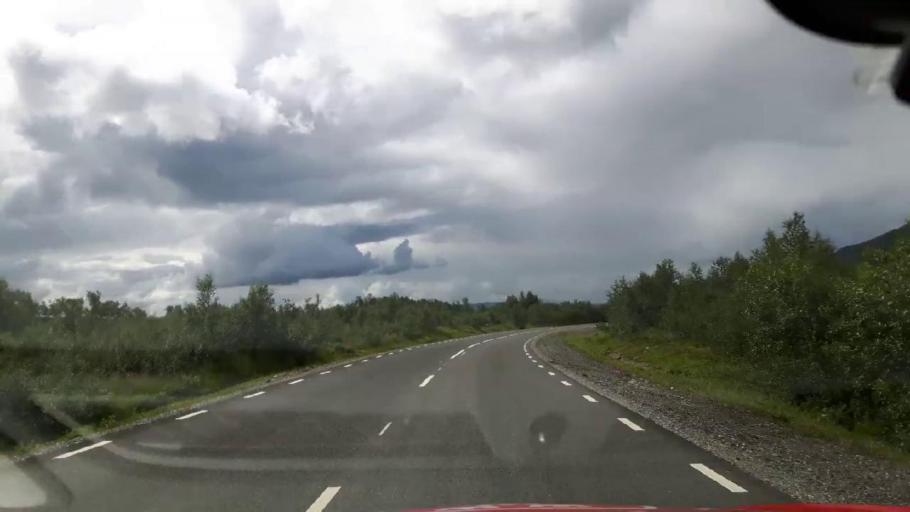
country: NO
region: Nordland
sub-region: Hattfjelldal
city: Hattfjelldal
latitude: 64.9968
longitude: 14.2385
